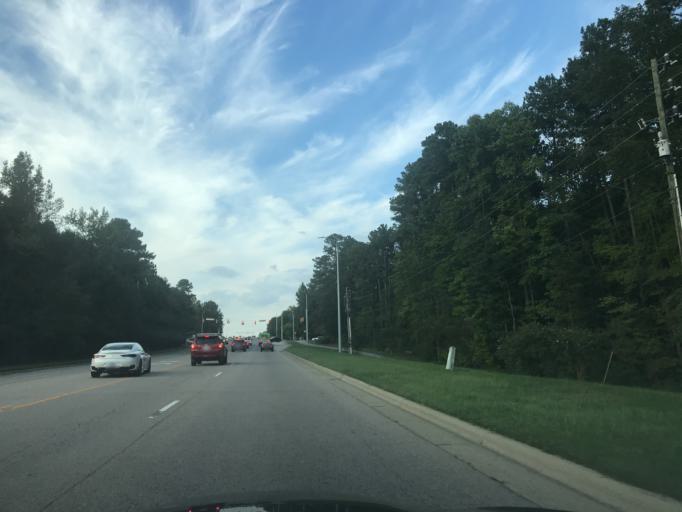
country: US
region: North Carolina
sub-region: Wake County
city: Green Level
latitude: 35.7823
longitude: -78.8716
